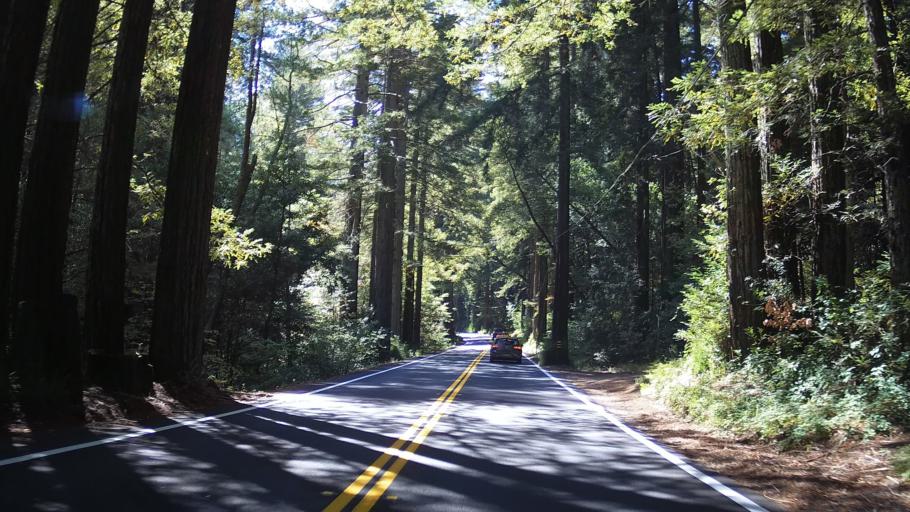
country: US
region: California
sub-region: Marin County
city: Lagunitas-Forest Knolls
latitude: 38.0197
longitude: -122.7256
